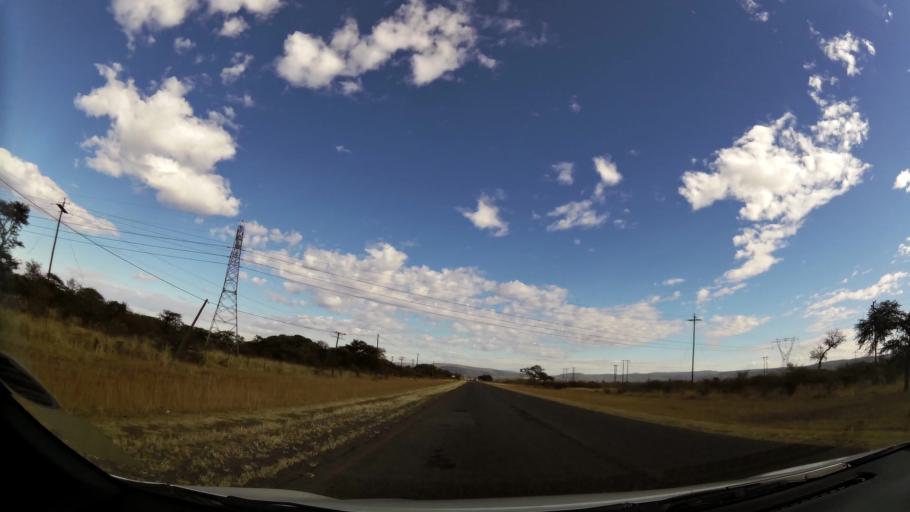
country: ZA
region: Limpopo
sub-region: Waterberg District Municipality
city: Bela-Bela
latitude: -24.9001
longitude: 28.3279
